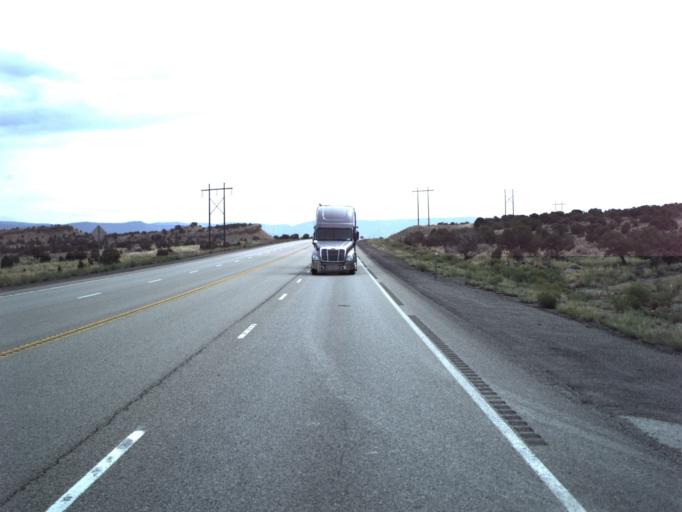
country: US
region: Utah
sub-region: Carbon County
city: Wellington
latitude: 39.5469
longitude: -110.6325
